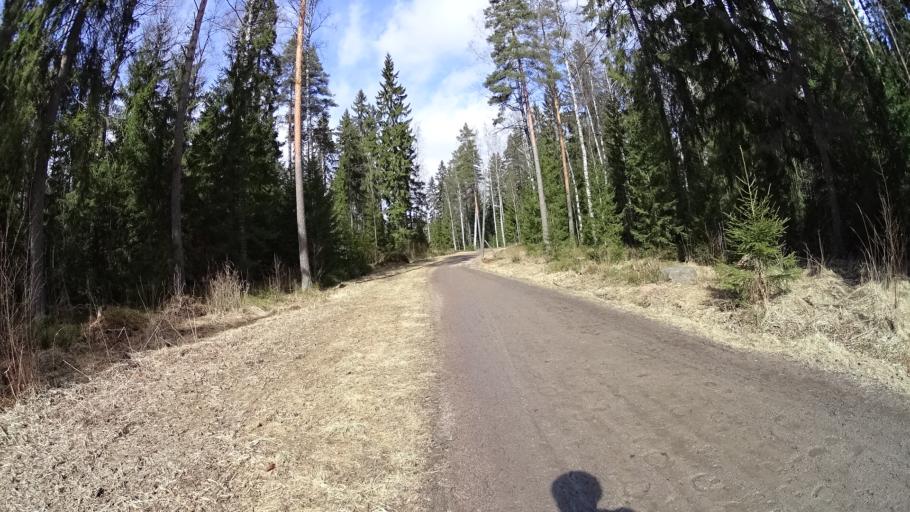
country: FI
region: Uusimaa
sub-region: Helsinki
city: Kilo
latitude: 60.2976
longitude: 24.8165
